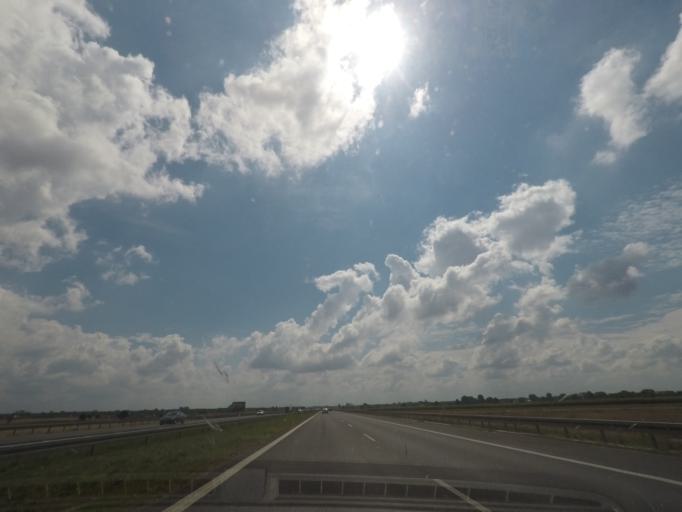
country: PL
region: Lodz Voivodeship
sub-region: Powiat zgierski
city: Strykow
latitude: 51.9718
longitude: 19.5743
